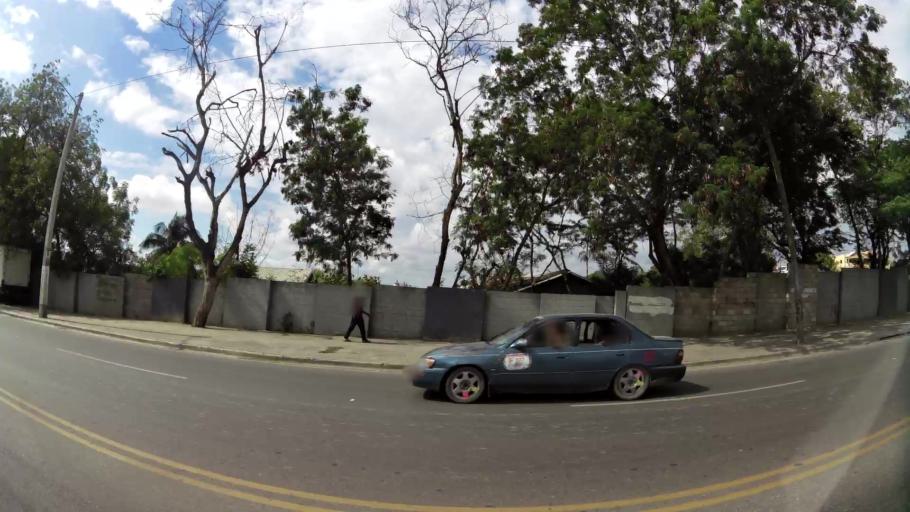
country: DO
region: Santiago
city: Santiago de los Caballeros
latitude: 19.4751
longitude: -70.7221
